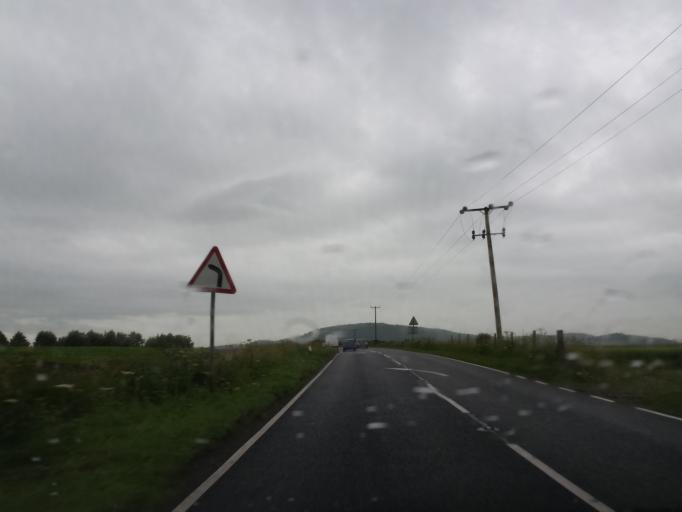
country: GB
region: Scotland
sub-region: Fife
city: Balmullo
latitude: 56.4075
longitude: -2.9141
